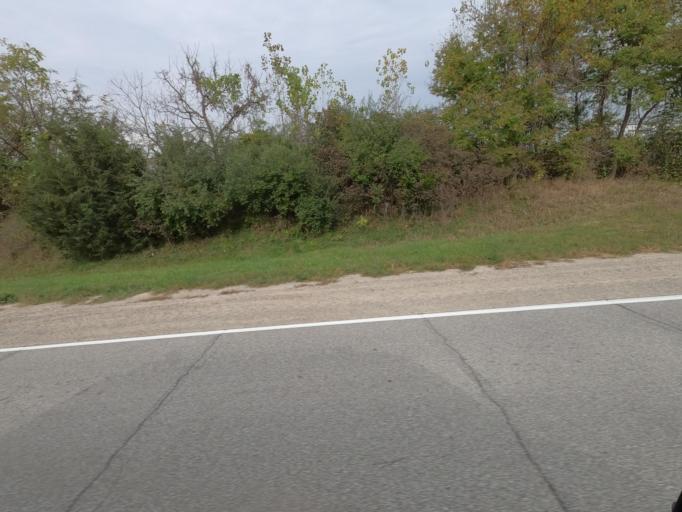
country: US
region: Iowa
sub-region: Van Buren County
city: Keosauqua
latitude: 40.8654
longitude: -92.1416
